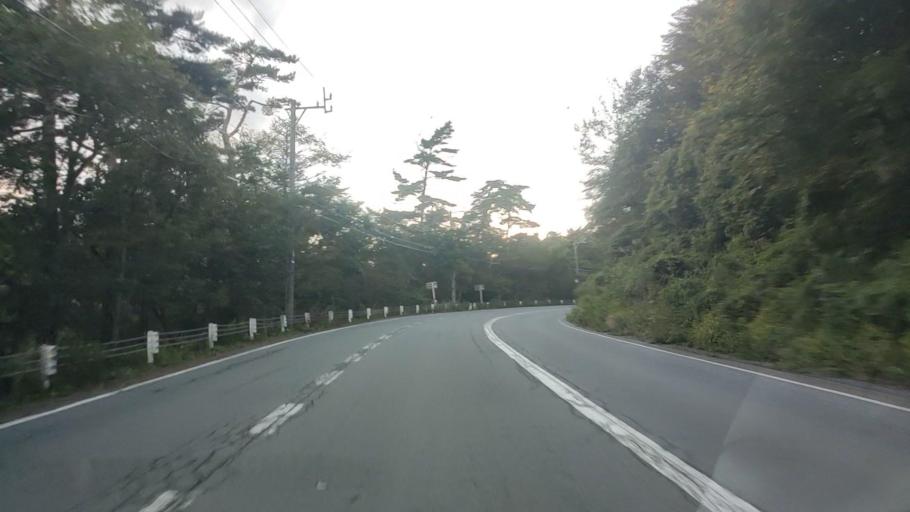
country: JP
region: Nagano
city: Komoro
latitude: 36.3950
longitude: 138.5806
